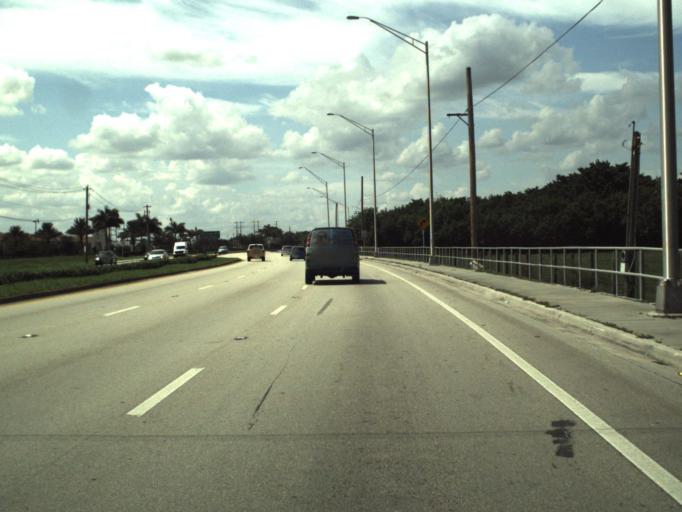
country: US
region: Florida
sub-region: Broward County
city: Davie
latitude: 26.0399
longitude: -80.2494
